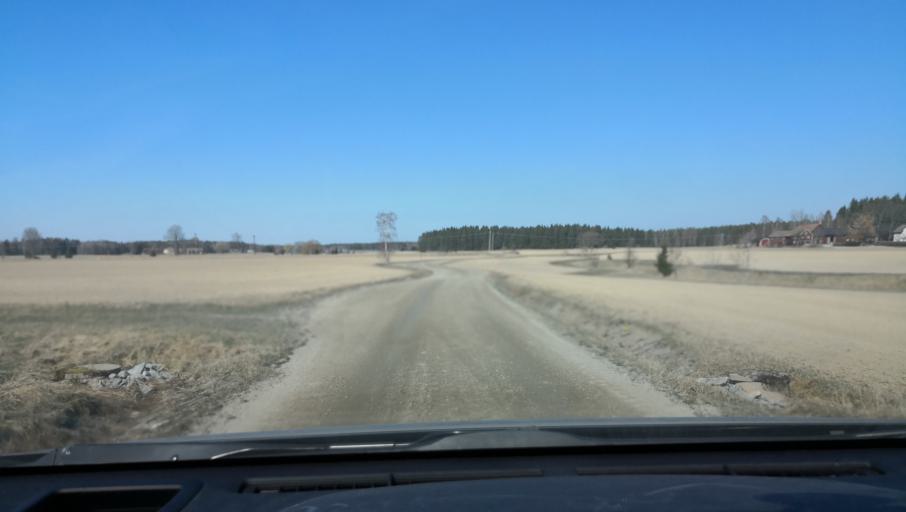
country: SE
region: Vaestmanland
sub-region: Sala Kommun
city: Sala
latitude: 59.8913
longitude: 16.5287
